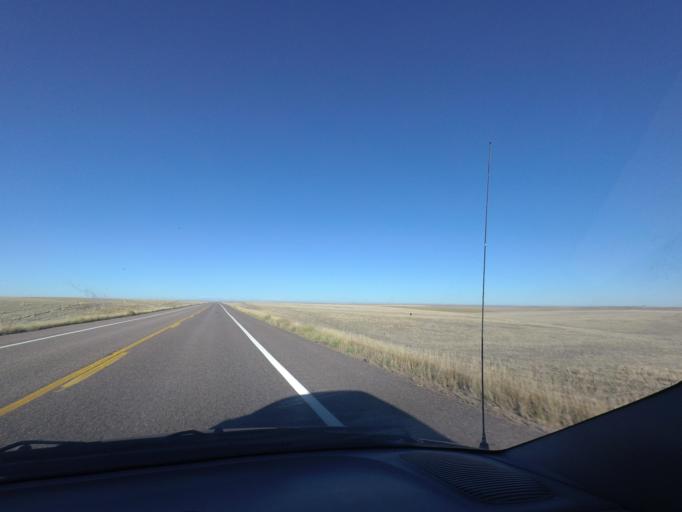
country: US
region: Colorado
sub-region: Arapahoe County
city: Byers
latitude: 39.7323
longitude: -103.9360
